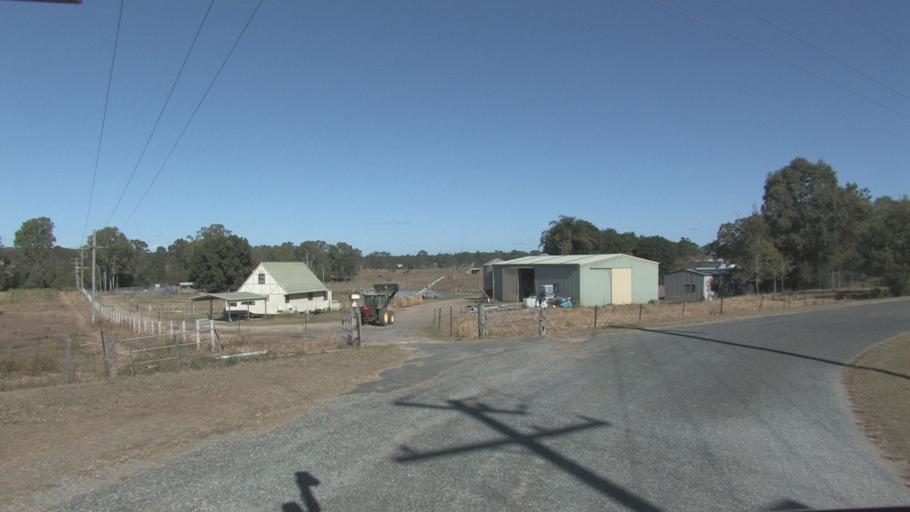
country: AU
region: Queensland
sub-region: Logan
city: Chambers Flat
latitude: -27.7631
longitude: 153.0904
